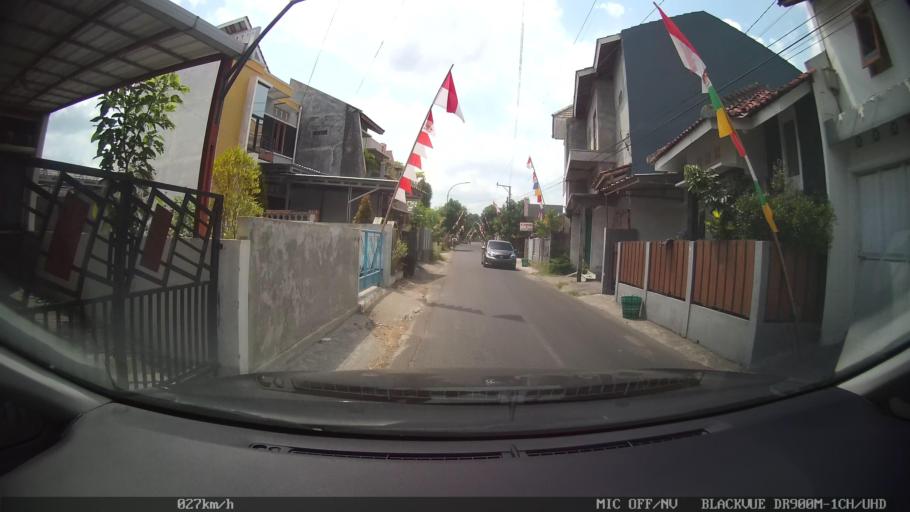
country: ID
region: Daerah Istimewa Yogyakarta
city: Kasihan
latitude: -7.8159
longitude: 110.3403
